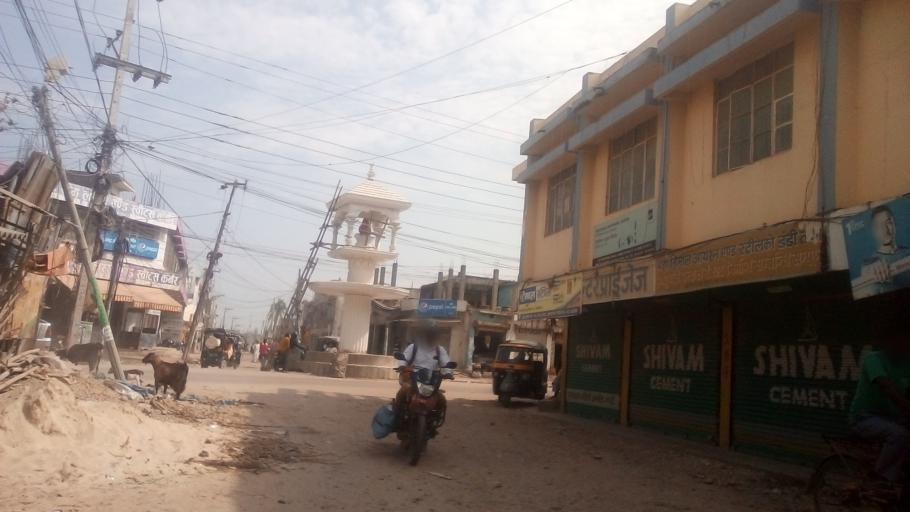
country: NP
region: Central Region
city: Janakpur
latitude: 26.7356
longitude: 85.9318
